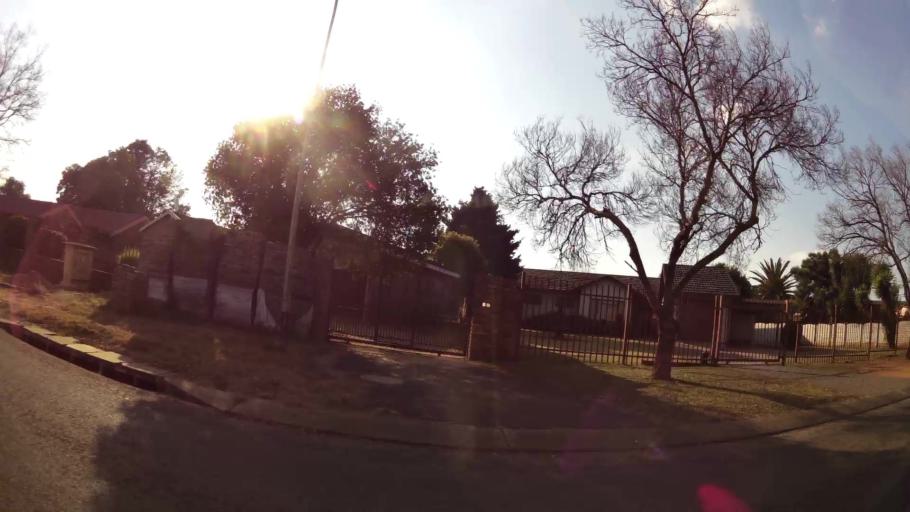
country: ZA
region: Gauteng
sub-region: Ekurhuleni Metropolitan Municipality
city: Tembisa
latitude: -25.9582
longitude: 28.2220
